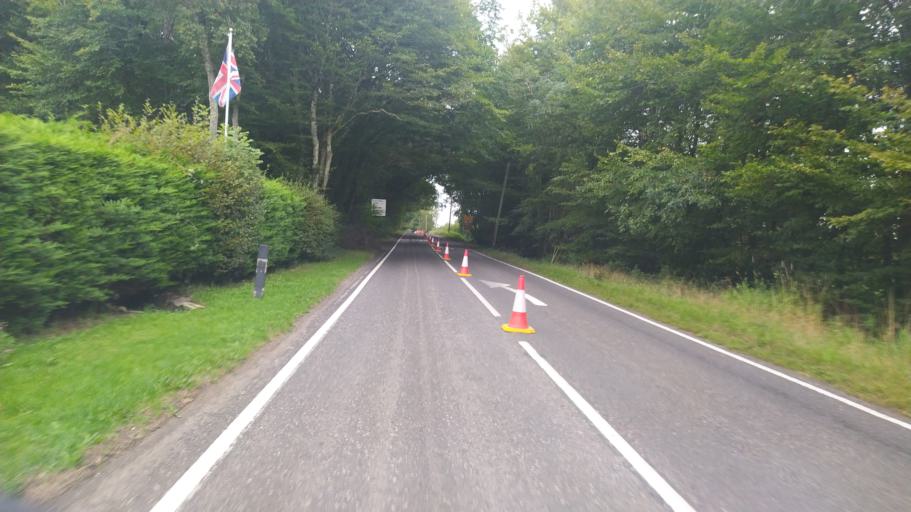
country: GB
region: England
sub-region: Dorset
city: Sherborne
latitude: 50.8769
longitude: -2.4828
